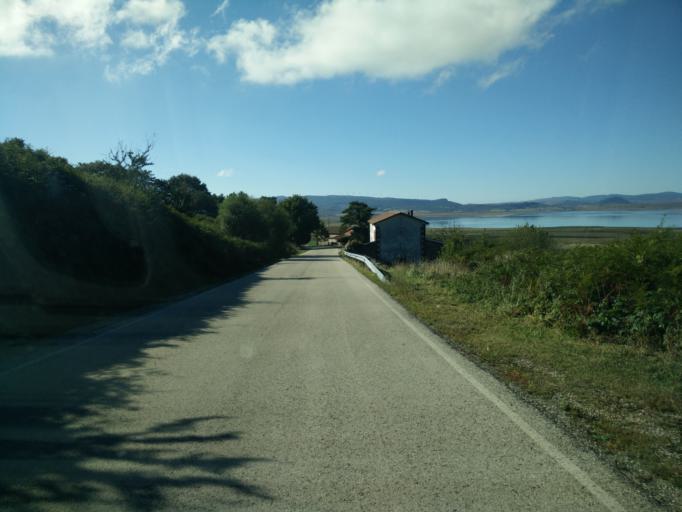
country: ES
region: Castille and Leon
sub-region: Provincia de Burgos
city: Arija
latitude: 43.0309
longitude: -3.8602
